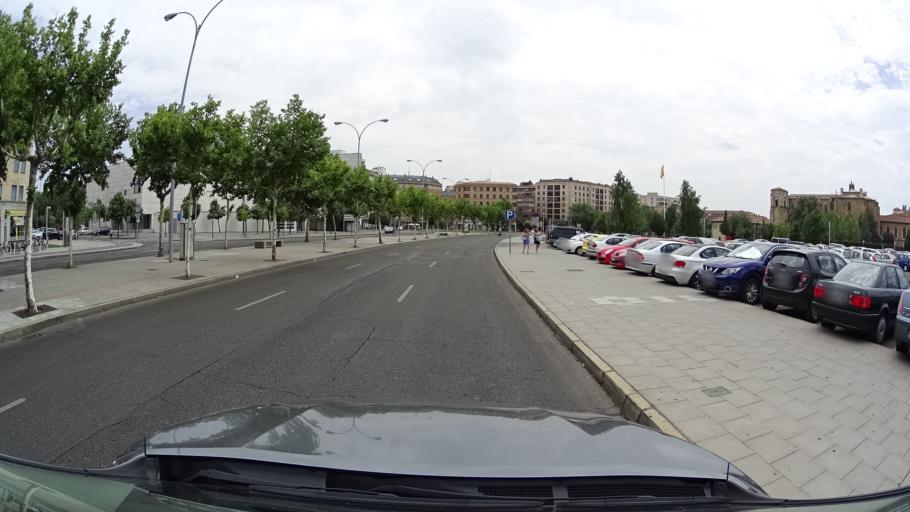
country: ES
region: Castille and Leon
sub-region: Provincia de Leon
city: Leon
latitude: 42.6035
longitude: -5.5799
